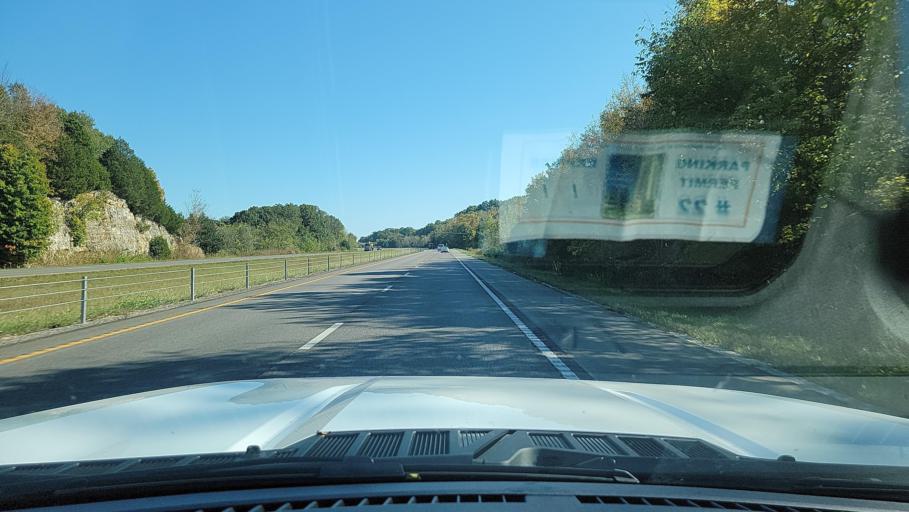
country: US
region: Missouri
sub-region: Jefferson County
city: Crystal City
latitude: 38.0387
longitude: -90.2601
